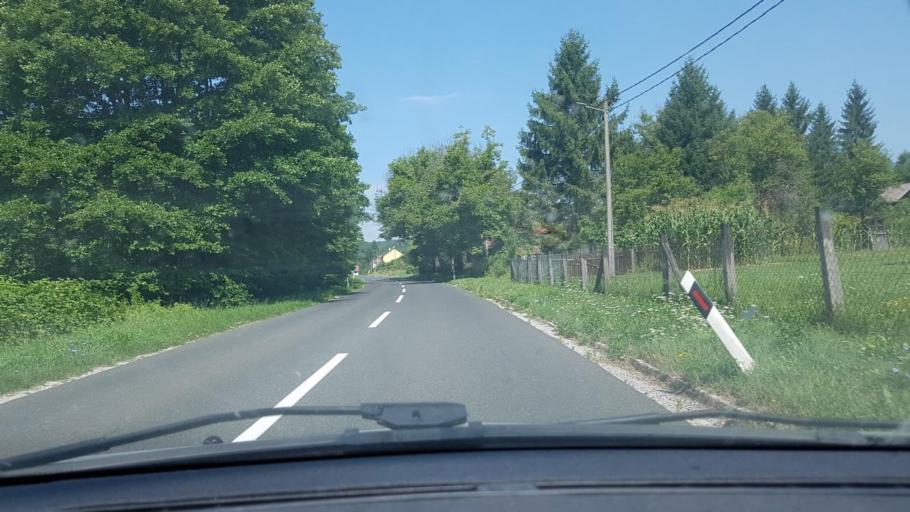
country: HR
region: Karlovacka
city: Vojnic
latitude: 45.2410
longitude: 15.7341
